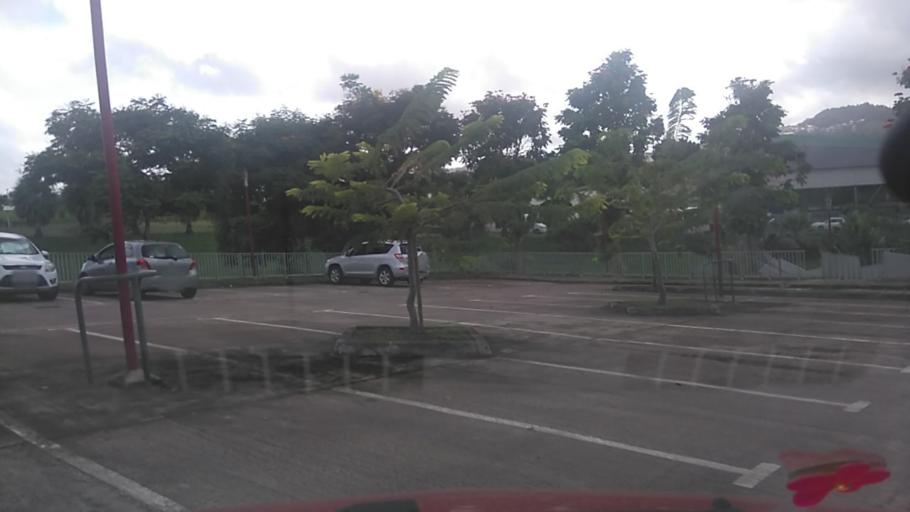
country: MQ
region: Martinique
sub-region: Martinique
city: Le Lamentin
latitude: 14.6276
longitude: -60.9881
